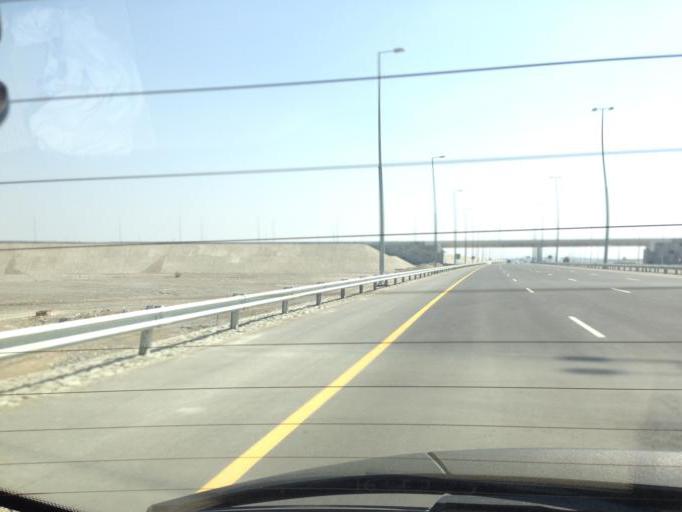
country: OM
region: Al Batinah
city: Barka'
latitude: 23.5754
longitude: 57.7340
